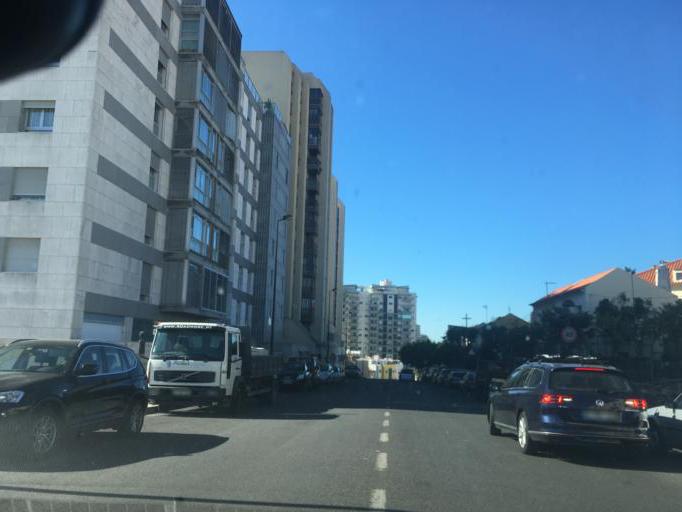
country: PT
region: Lisbon
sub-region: Oeiras
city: Alges
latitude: 38.7109
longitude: -9.2046
